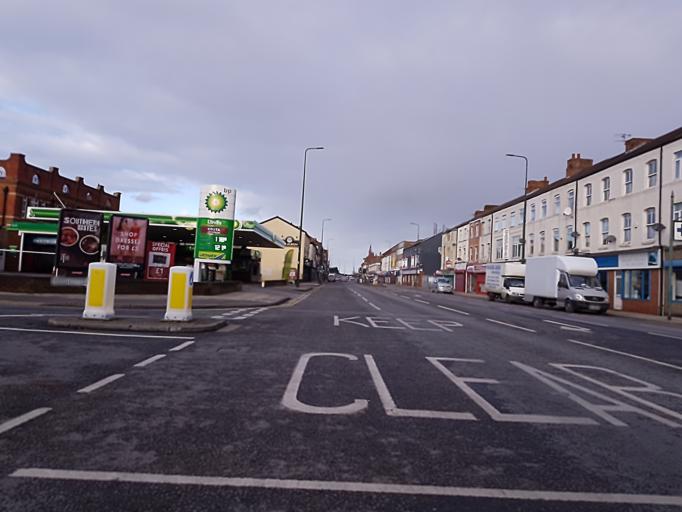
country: GB
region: England
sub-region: North East Lincolnshire
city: Grimsby
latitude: 53.5744
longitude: -0.0678
